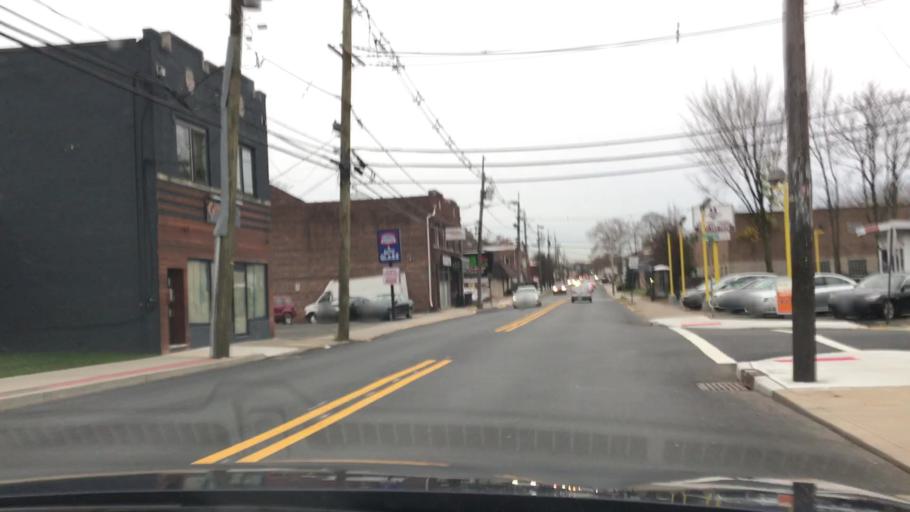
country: US
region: New Jersey
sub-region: Bergen County
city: Bergenfield
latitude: 40.9203
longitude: -73.9968
